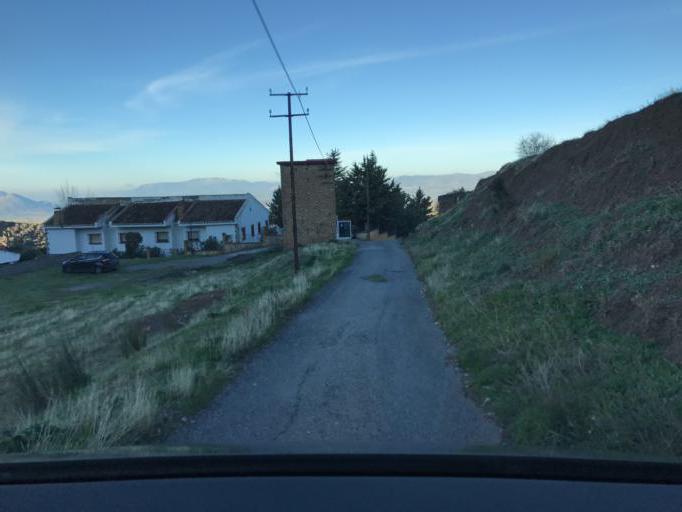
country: ES
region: Andalusia
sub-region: Provincia de Granada
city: Nivar
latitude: 37.2659
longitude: -3.5729
